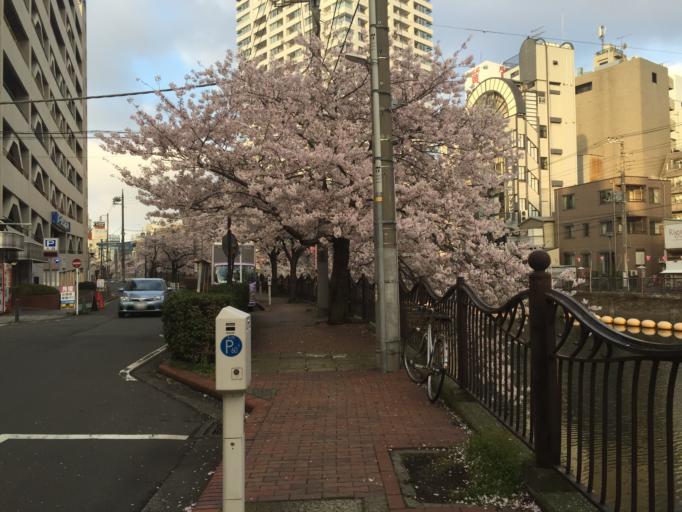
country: JP
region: Kanagawa
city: Yokohama
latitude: 35.4458
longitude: 139.6290
